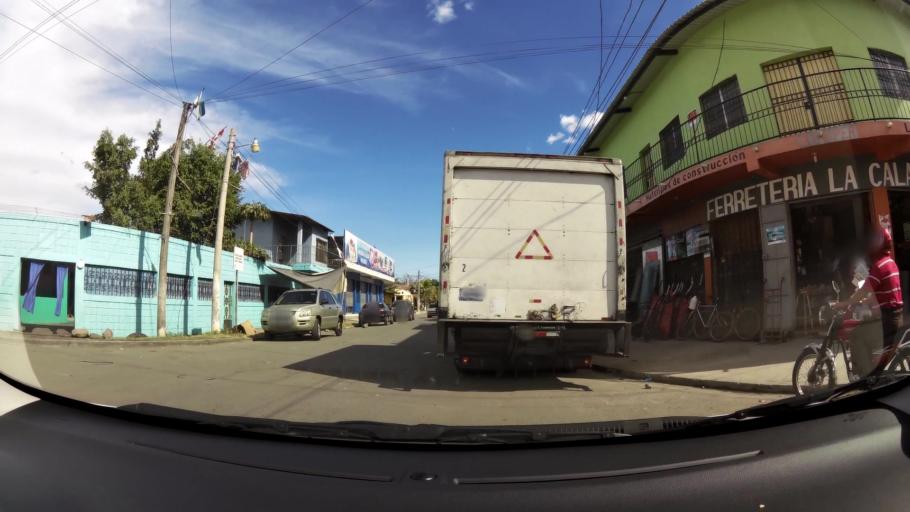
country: SV
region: San Salvador
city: Aguilares
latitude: 13.9592
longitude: -89.1863
